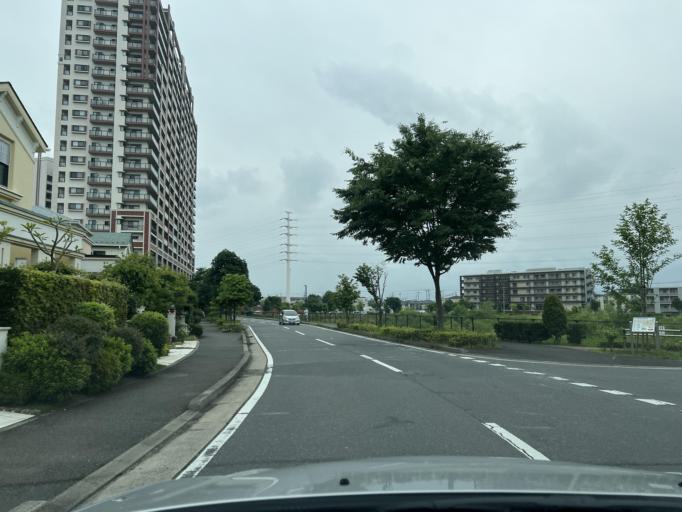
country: JP
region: Chiba
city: Nagareyama
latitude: 35.8679
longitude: 139.9216
